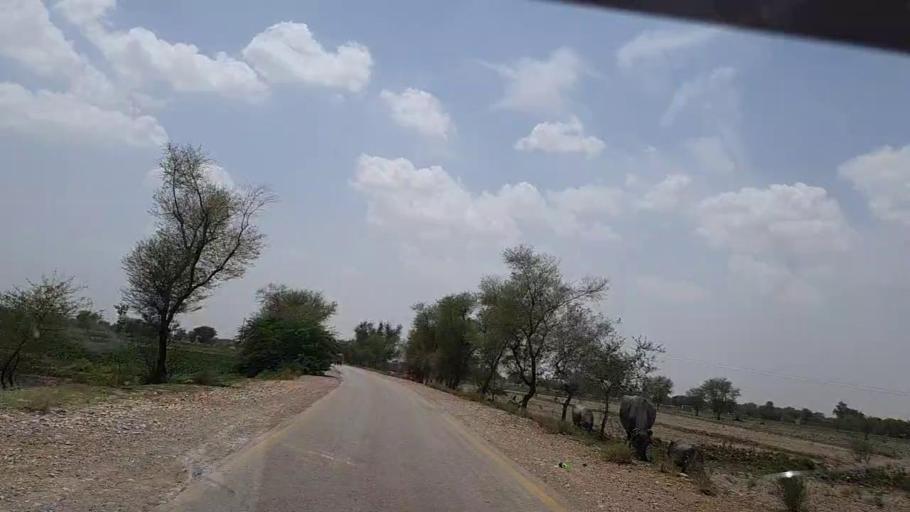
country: PK
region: Sindh
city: Bhan
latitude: 26.5412
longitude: 67.6814
